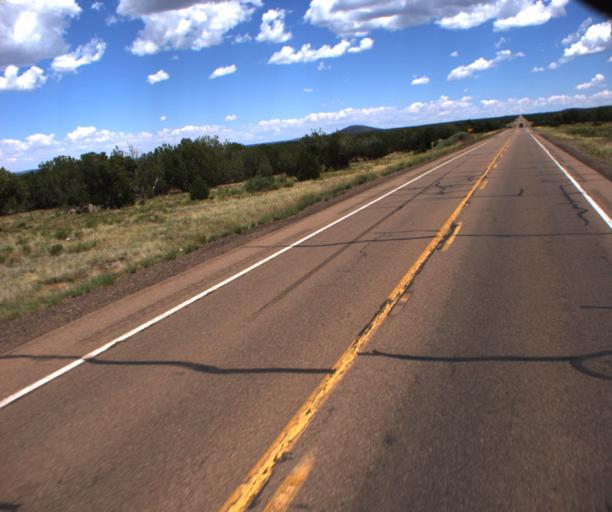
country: US
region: Arizona
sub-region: Navajo County
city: Show Low
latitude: 34.2669
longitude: -109.9456
